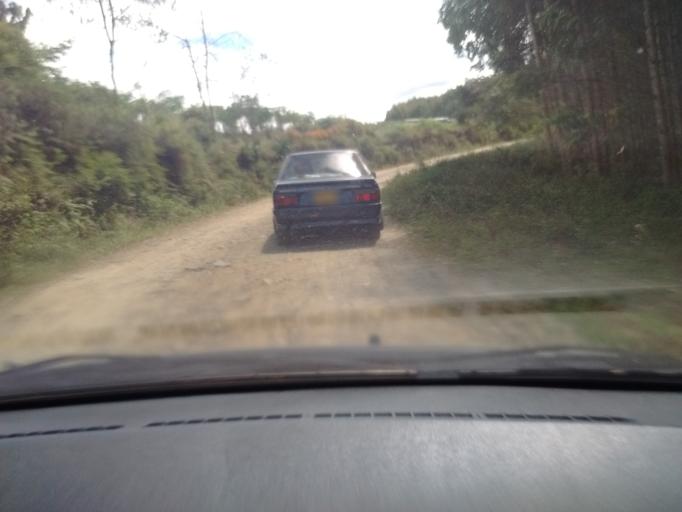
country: CO
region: Cauca
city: El Tambo
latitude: 2.4693
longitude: -76.8263
